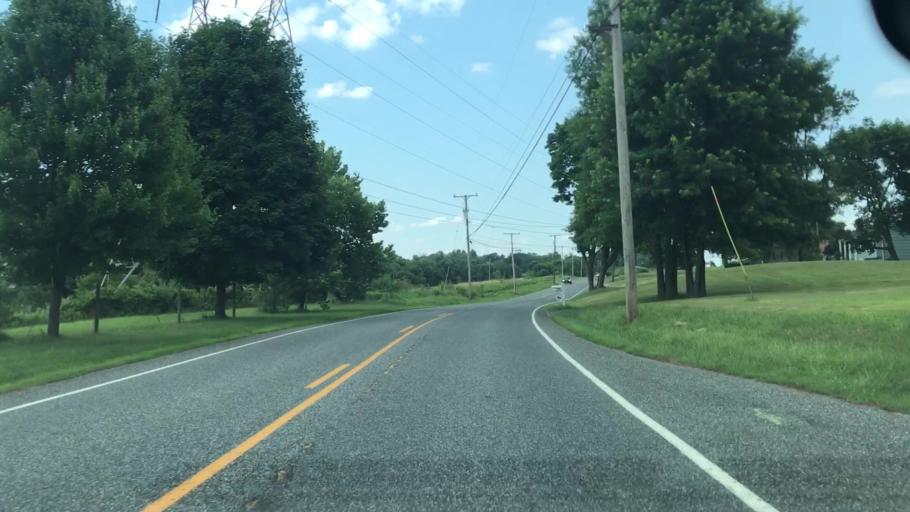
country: US
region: New Jersey
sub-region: Hunterdon County
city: Flemington
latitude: 40.4916
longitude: -74.8119
